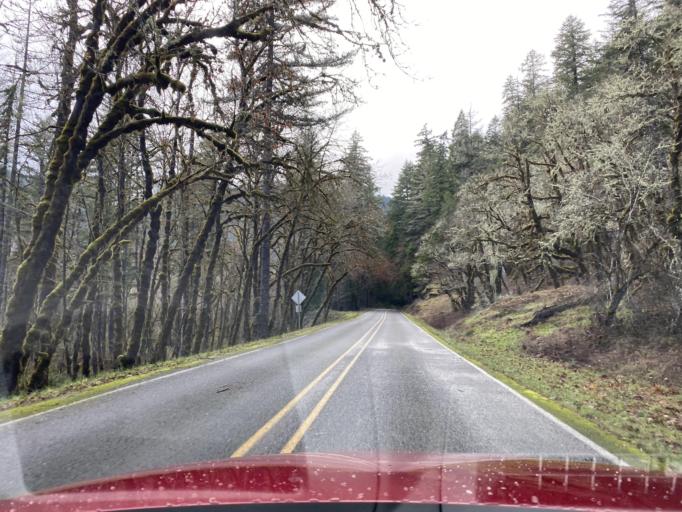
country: US
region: Oregon
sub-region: Lane County
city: Oakridge
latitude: 43.7479
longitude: -122.5170
